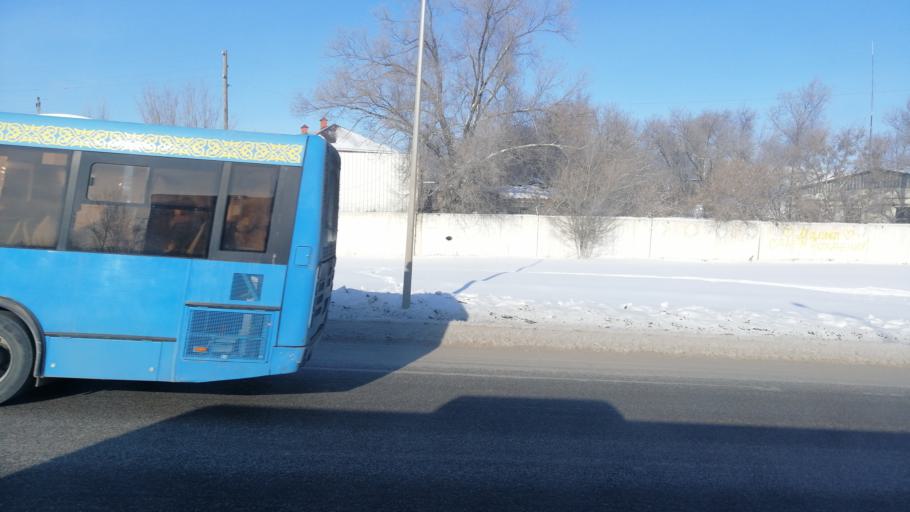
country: KZ
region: Aqtoebe
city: Aqtobe
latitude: 50.2963
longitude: 57.1828
